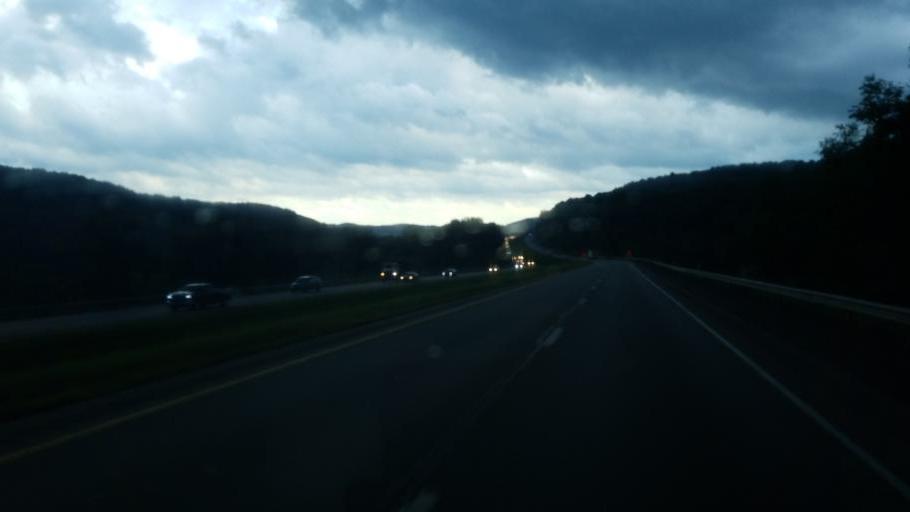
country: US
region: Pennsylvania
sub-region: Butler County
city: Prospect
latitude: 40.8774
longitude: -80.1142
